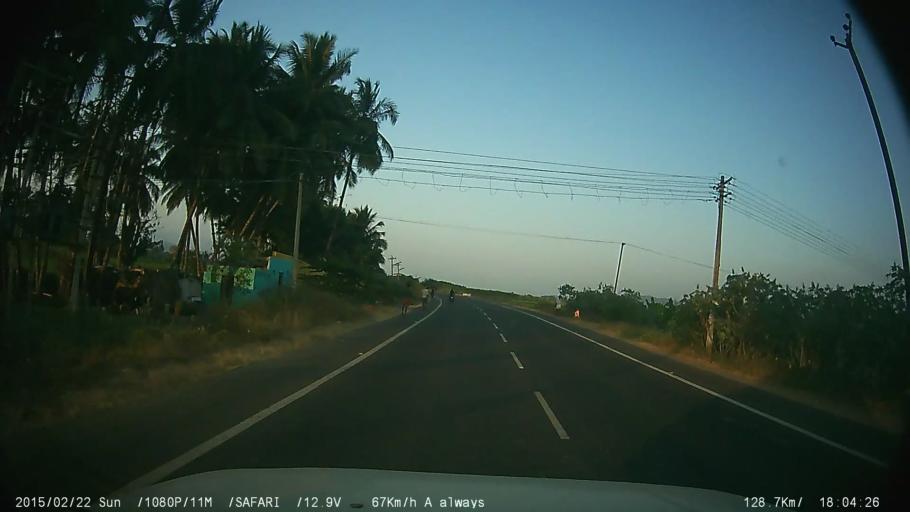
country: IN
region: Tamil Nadu
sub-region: Theni
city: Uttamapalaiyam
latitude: 9.8156
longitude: 77.3496
